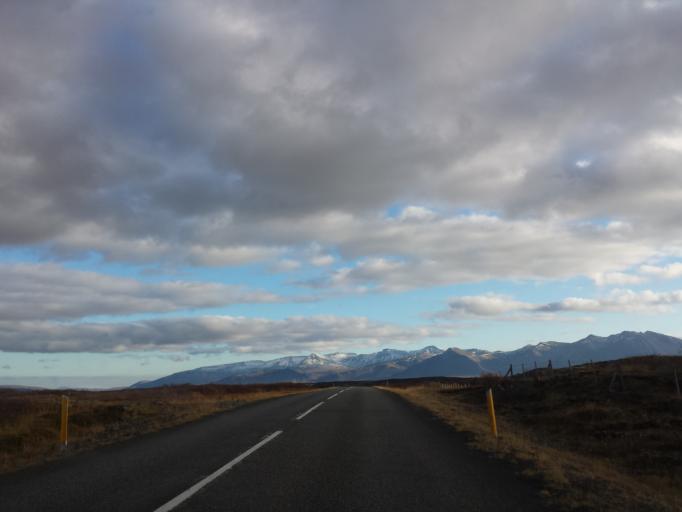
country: IS
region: West
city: Borgarnes
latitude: 64.5994
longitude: -22.0181
